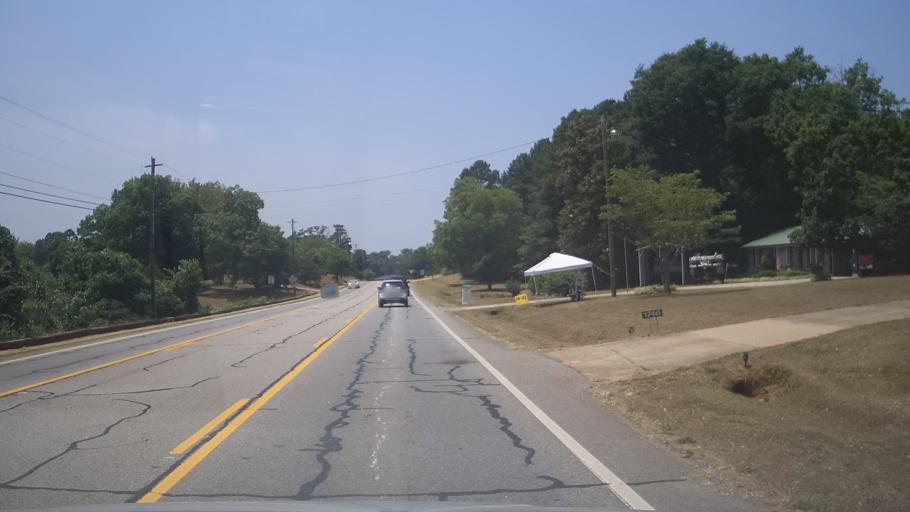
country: US
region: Georgia
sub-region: Hart County
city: Royston
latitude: 34.2856
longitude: -83.1396
